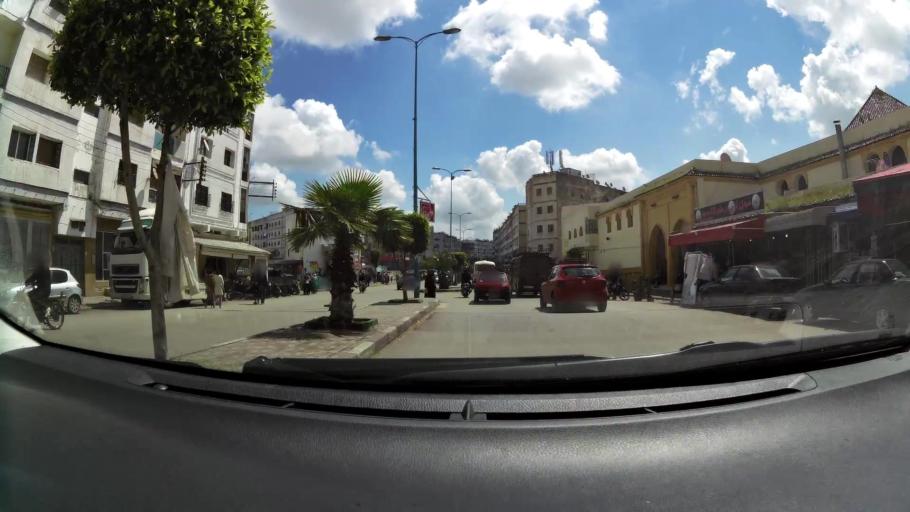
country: MA
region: Grand Casablanca
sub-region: Mediouna
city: Tit Mellil
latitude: 33.5385
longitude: -7.5551
